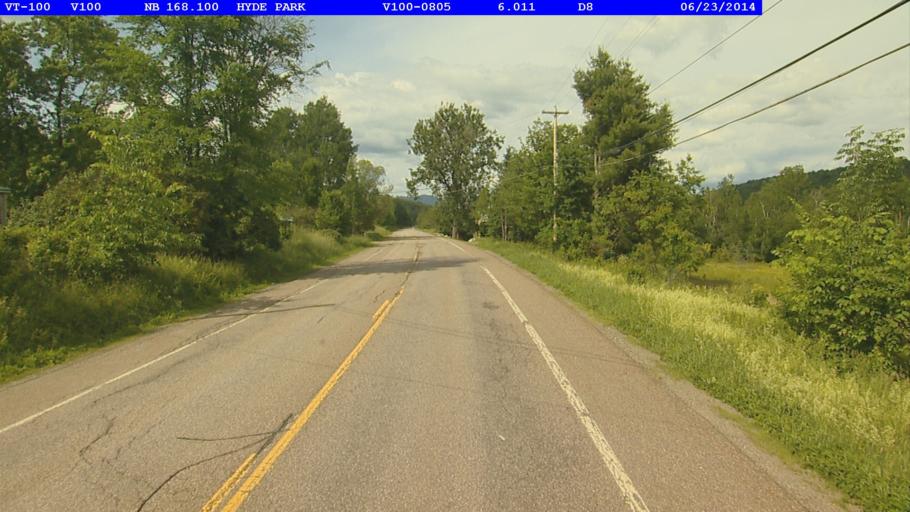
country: US
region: Vermont
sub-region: Lamoille County
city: Hyde Park
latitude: 44.6770
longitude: -72.5942
